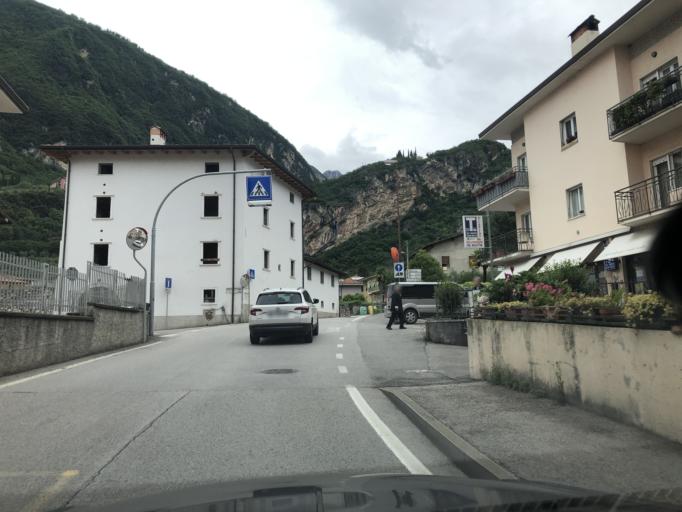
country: IT
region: Trentino-Alto Adige
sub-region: Provincia di Trento
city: Tenno
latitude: 45.9087
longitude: 10.8421
